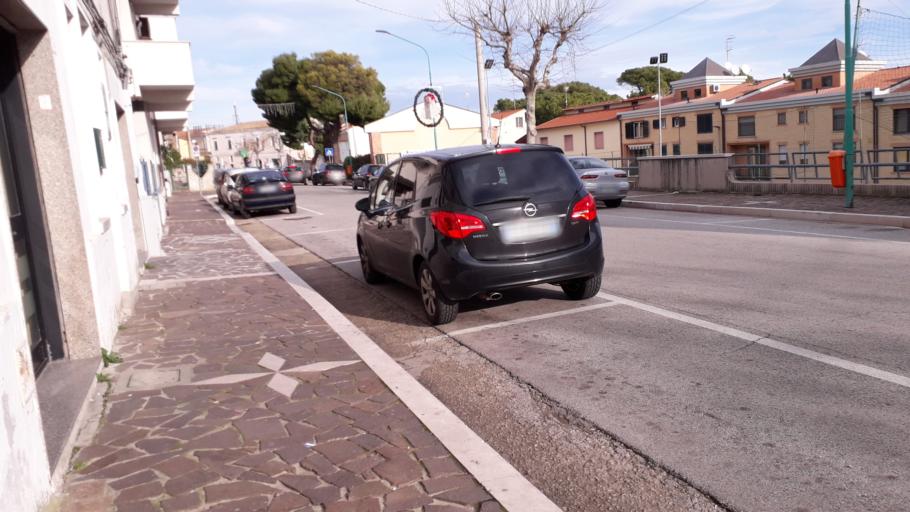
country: IT
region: Molise
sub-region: Provincia di Campobasso
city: Campomarino
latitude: 41.9555
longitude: 15.0355
